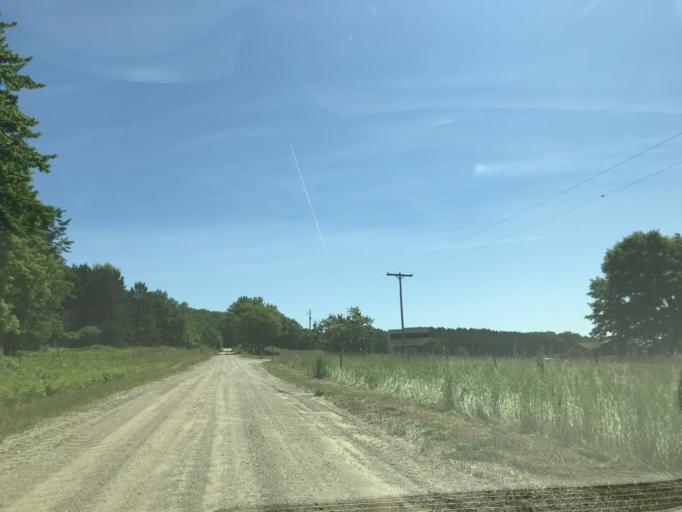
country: US
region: Michigan
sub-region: Missaukee County
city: Lake City
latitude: 44.2790
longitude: -85.0435
